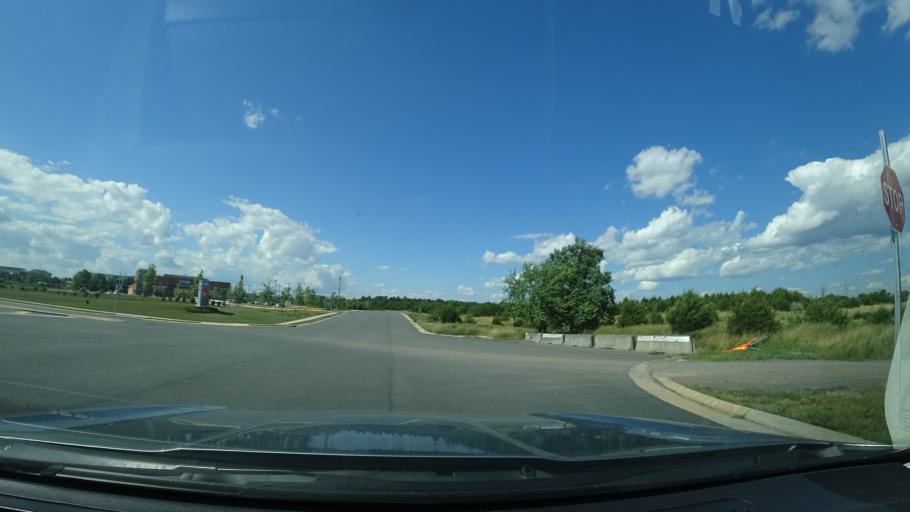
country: US
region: Virginia
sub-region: Loudoun County
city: Broadlands
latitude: 38.9930
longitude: -77.4802
